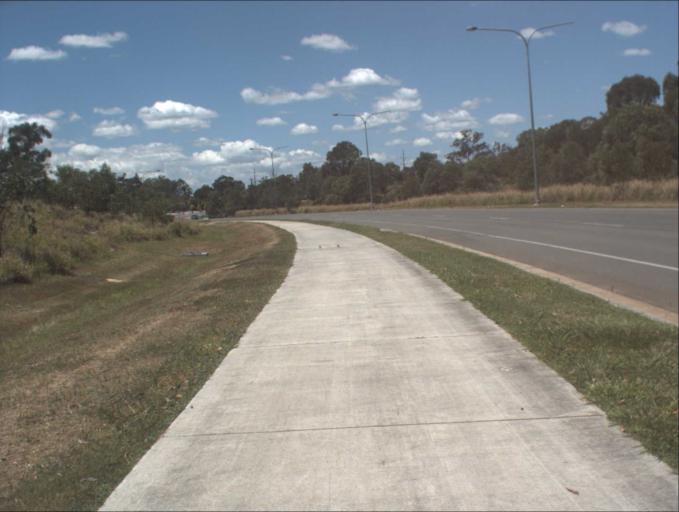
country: AU
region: Queensland
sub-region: Logan
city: Woodridge
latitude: -27.6546
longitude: 153.0893
